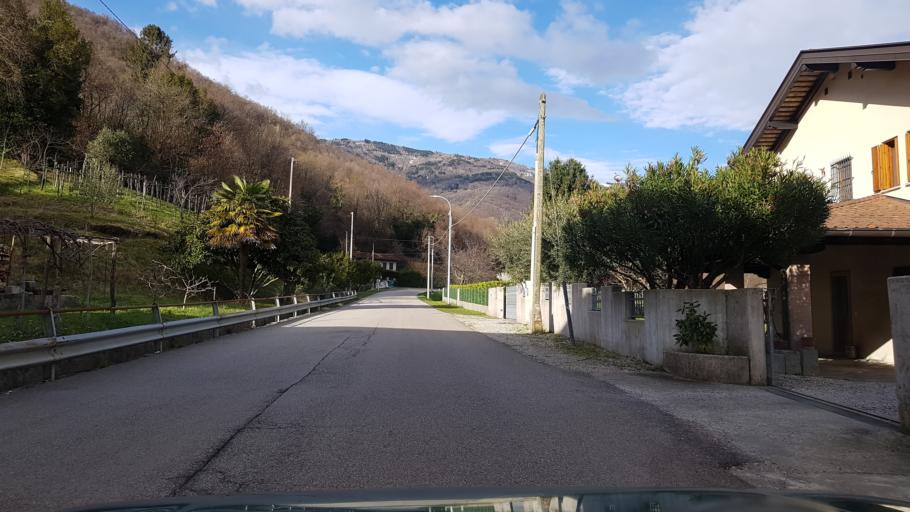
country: IT
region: Friuli Venezia Giulia
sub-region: Provincia di Udine
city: Faedis
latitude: 46.1589
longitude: 13.3529
